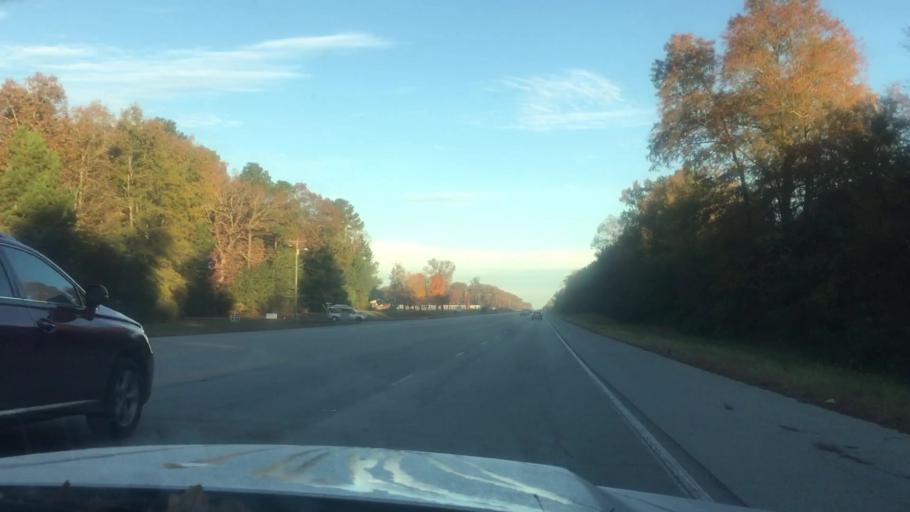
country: US
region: Tennessee
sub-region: Franklin County
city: Estill Springs
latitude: 35.2965
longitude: -86.1505
